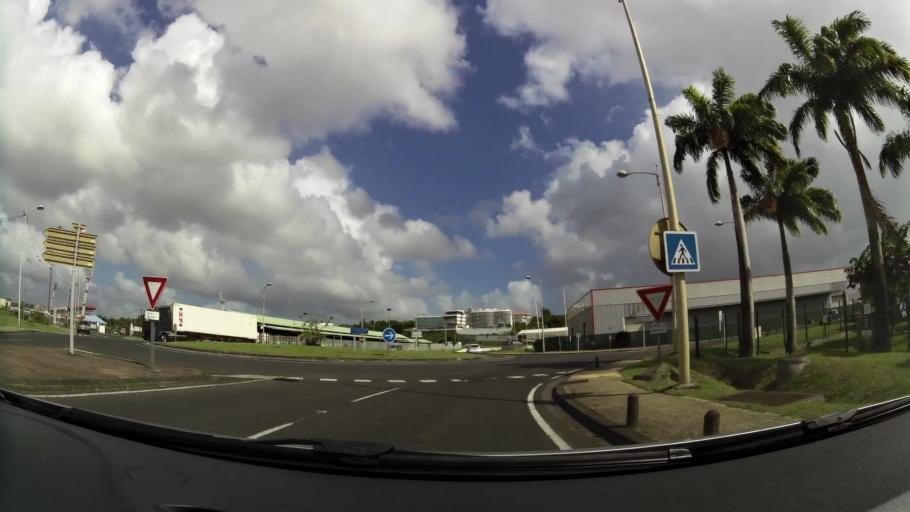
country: MQ
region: Martinique
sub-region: Martinique
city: Fort-de-France
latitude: 14.6005
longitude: -61.0488
